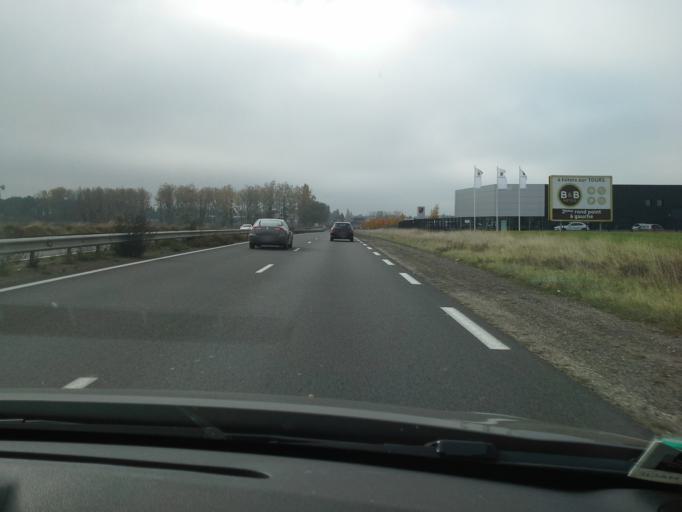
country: FR
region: Centre
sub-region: Departement d'Indre-et-Loire
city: Parcay-Meslay
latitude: 47.4443
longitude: 0.7218
